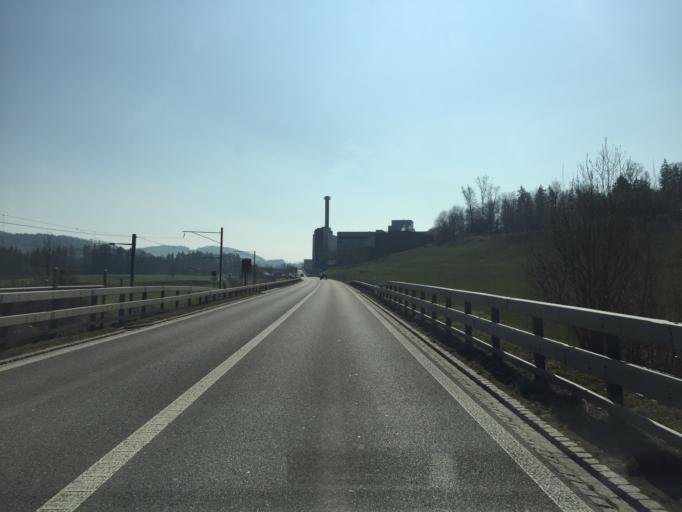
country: CH
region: Saint Gallen
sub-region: Wahlkreis Wil
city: Jonschwil
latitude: 47.4269
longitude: 9.0662
